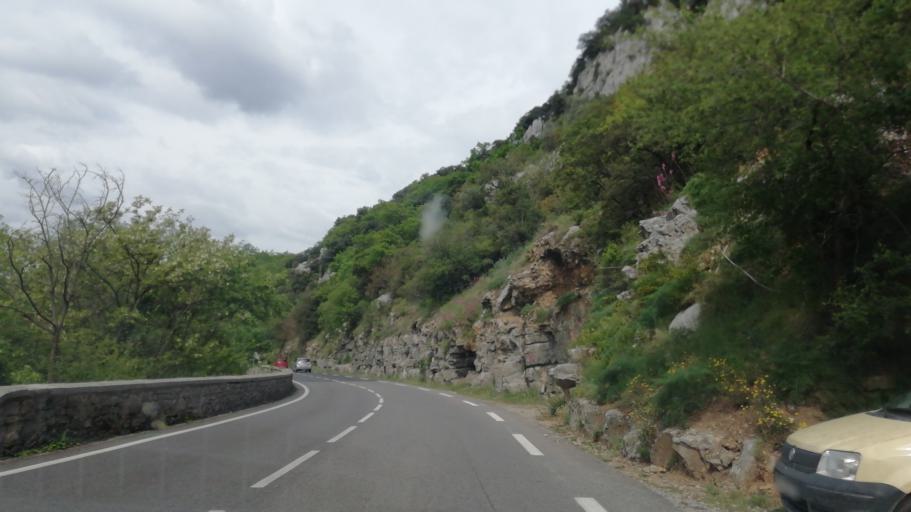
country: FR
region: Languedoc-Roussillon
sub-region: Departement de l'Herault
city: Laroque
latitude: 43.9166
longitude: 3.7340
